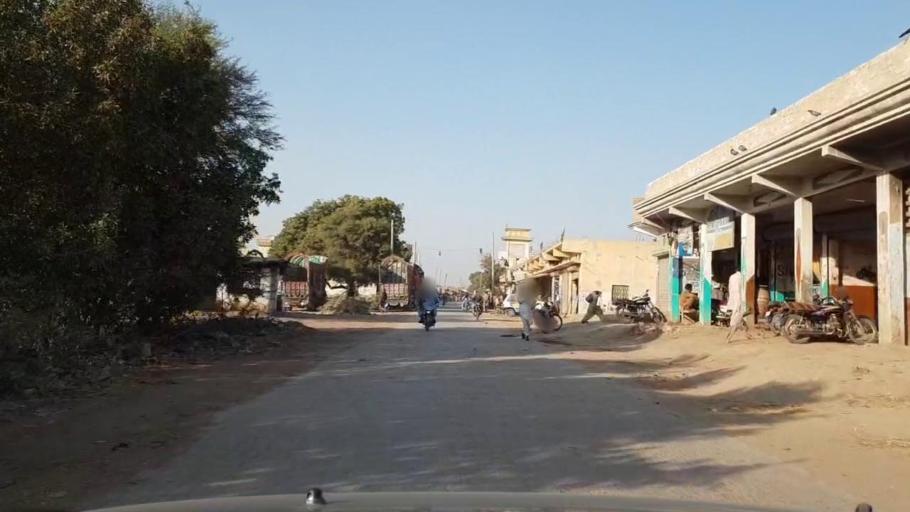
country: PK
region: Sindh
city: Chambar
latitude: 25.2153
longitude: 68.7796
